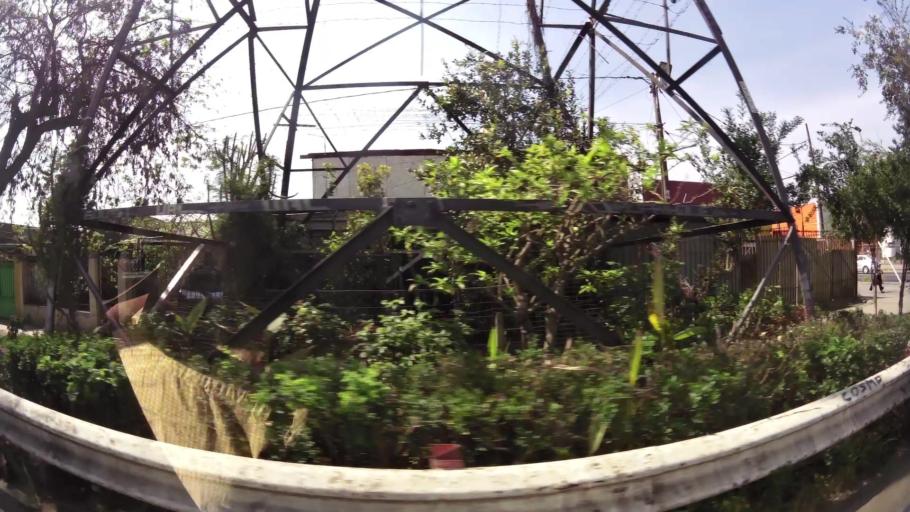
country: CL
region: Santiago Metropolitan
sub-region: Provincia de Santiago
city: Lo Prado
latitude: -33.4443
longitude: -70.7309
